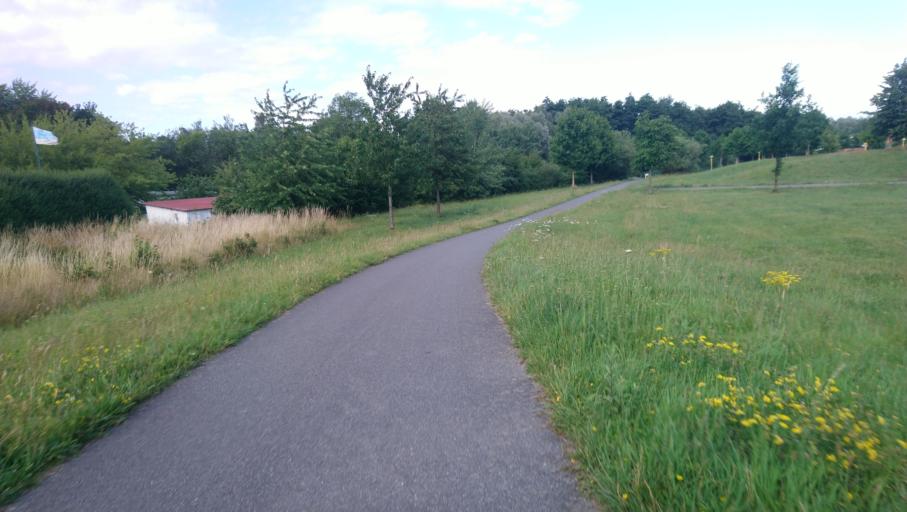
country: DE
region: Mecklenburg-Vorpommern
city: Papendorf
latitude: 54.0636
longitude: 12.1205
